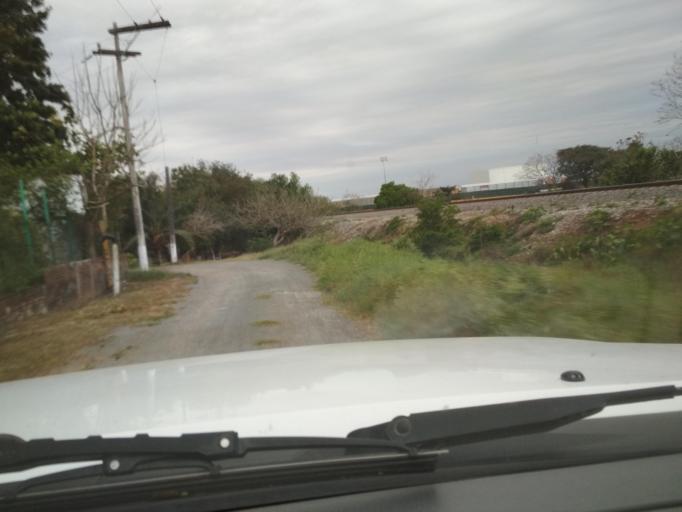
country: MX
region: Veracruz
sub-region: Veracruz
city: Delfino Victoria (Santa Fe)
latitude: 19.1665
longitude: -96.2602
